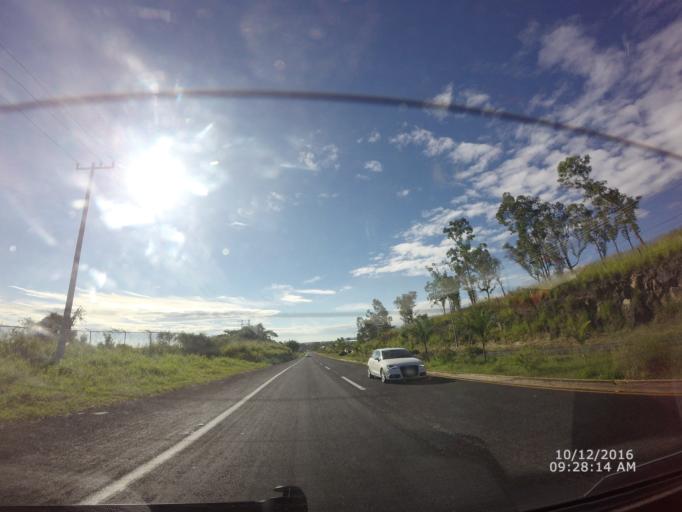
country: MX
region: Veracruz
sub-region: Emiliano Zapata
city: Dos Rios
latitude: 19.4986
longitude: -96.8216
